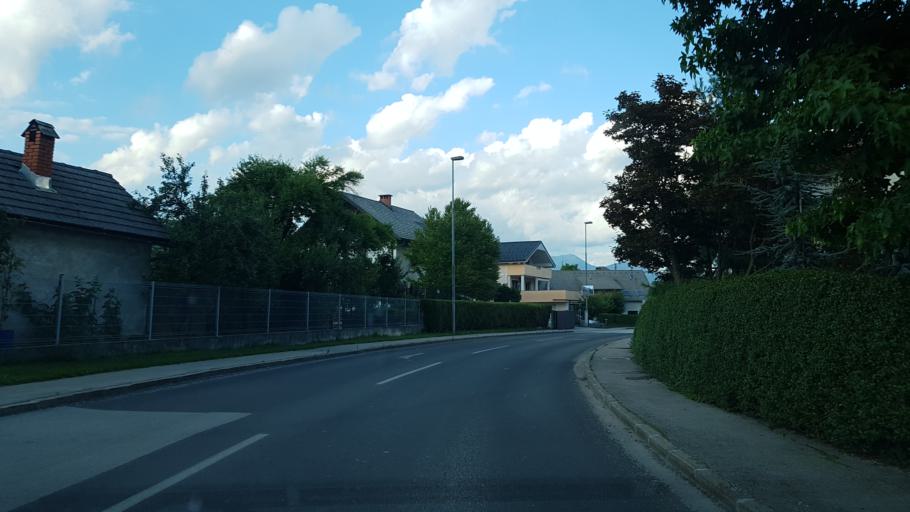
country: SI
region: Kranj
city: Zgornje Bitnje
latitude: 46.2298
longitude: 14.3403
